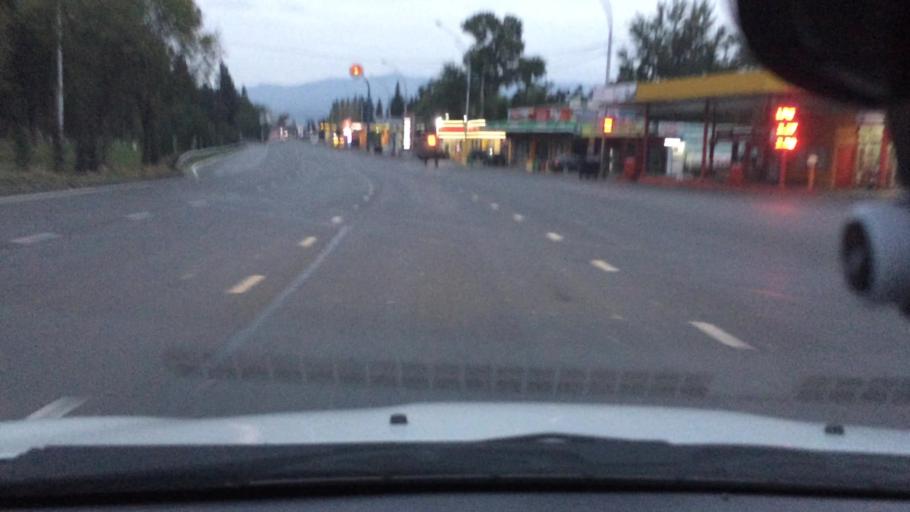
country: GE
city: Zahesi
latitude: 41.7664
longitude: 44.7692
